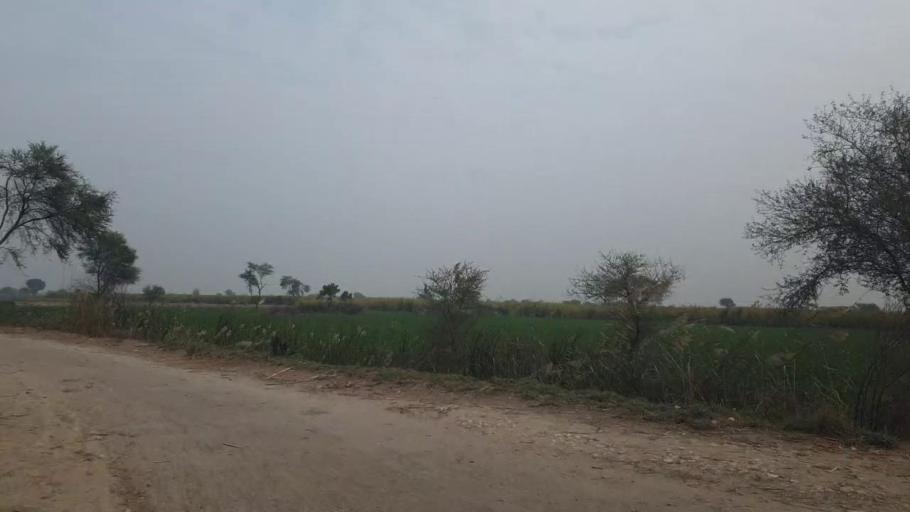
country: PK
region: Sindh
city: Tando Adam
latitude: 25.7242
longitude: 68.7385
